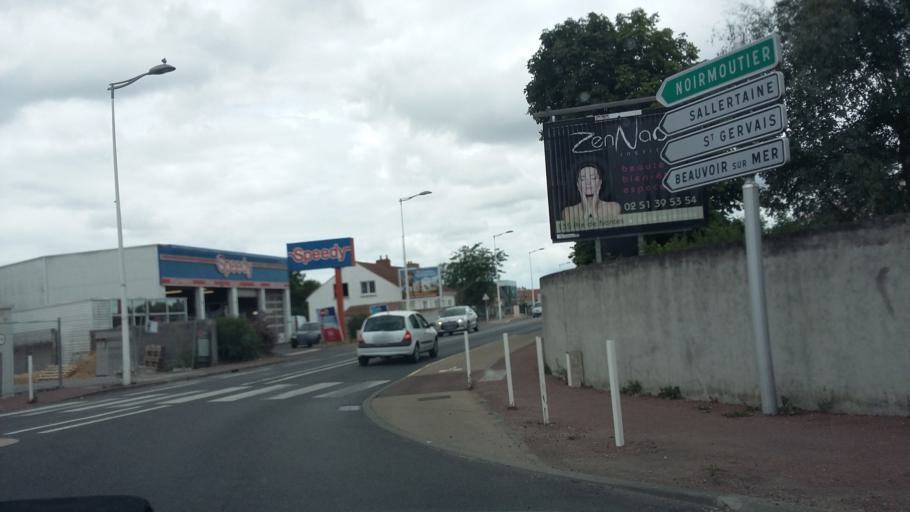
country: FR
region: Pays de la Loire
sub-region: Departement de la Vendee
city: Challans
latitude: 46.8530
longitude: -1.8927
